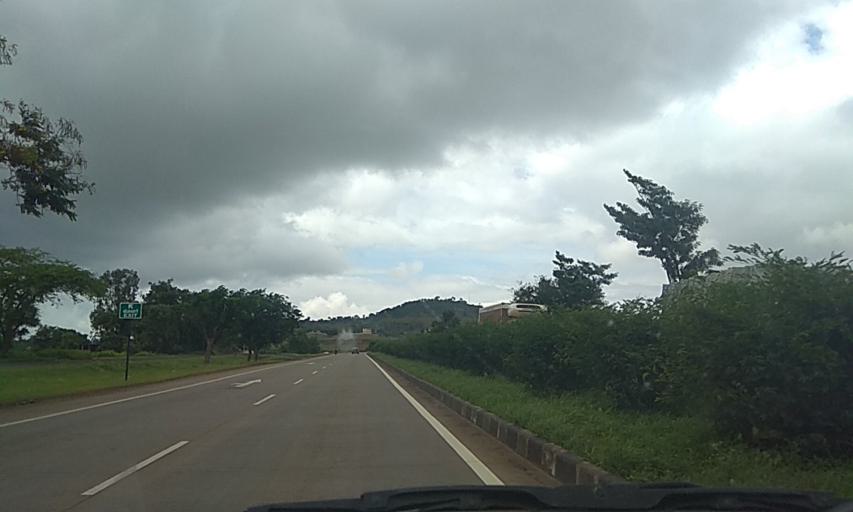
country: IN
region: Karnataka
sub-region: Belgaum
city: Sankeshwar
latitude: 16.2660
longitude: 74.4644
